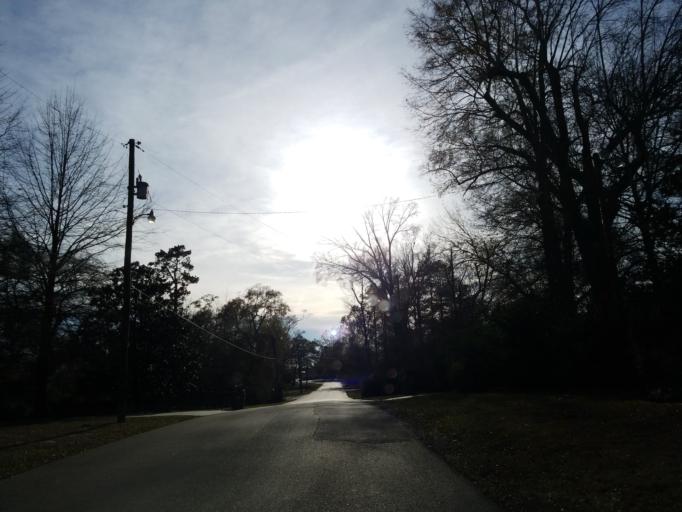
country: US
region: Mississippi
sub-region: Forrest County
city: Hattiesburg
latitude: 31.3198
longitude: -89.3008
